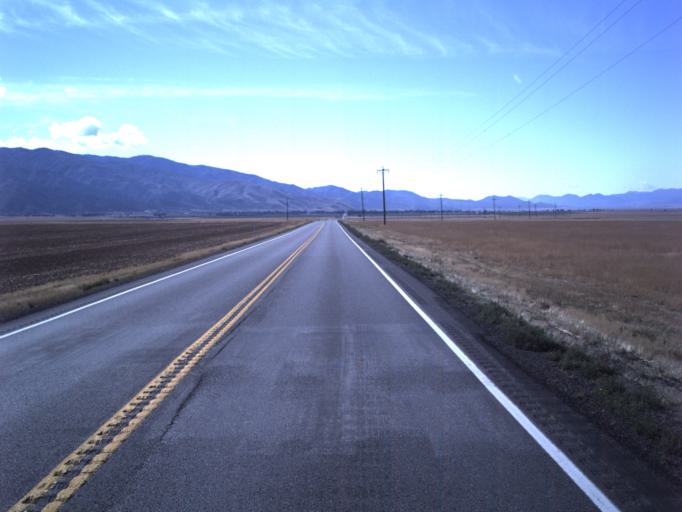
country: US
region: Utah
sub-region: Juab County
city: Nephi
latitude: 39.6128
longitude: -111.8618
